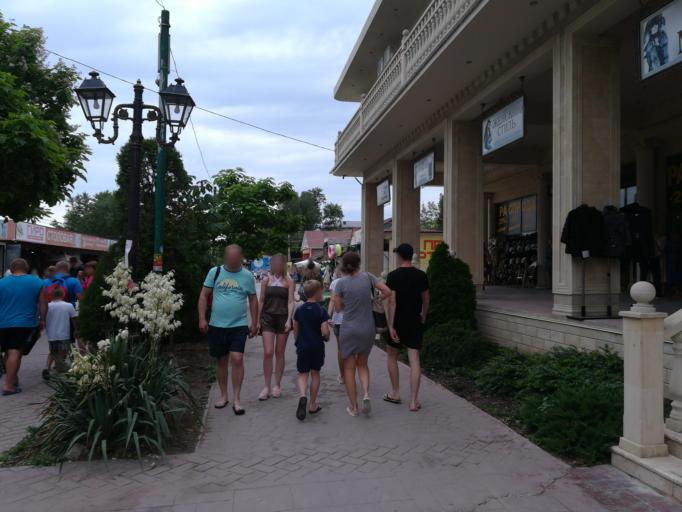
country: RU
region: Krasnodarskiy
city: Vityazevo
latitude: 44.9856
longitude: 37.2546
